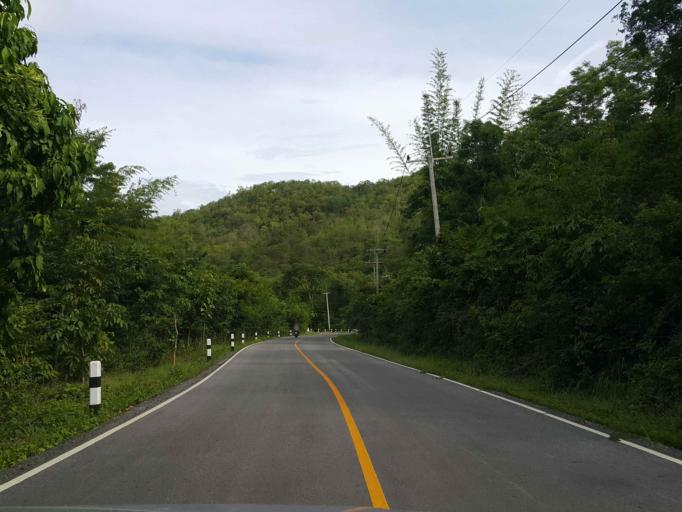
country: TH
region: Sukhothai
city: Thung Saliam
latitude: 17.2438
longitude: 99.4933
